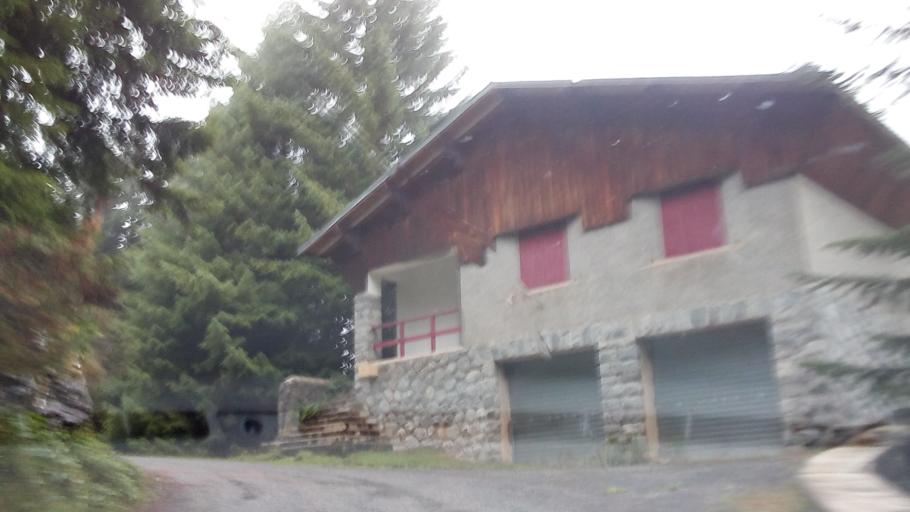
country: ES
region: Aragon
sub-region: Provincia de Huesca
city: Sallent de Gallego
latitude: 42.8843
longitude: -0.2712
